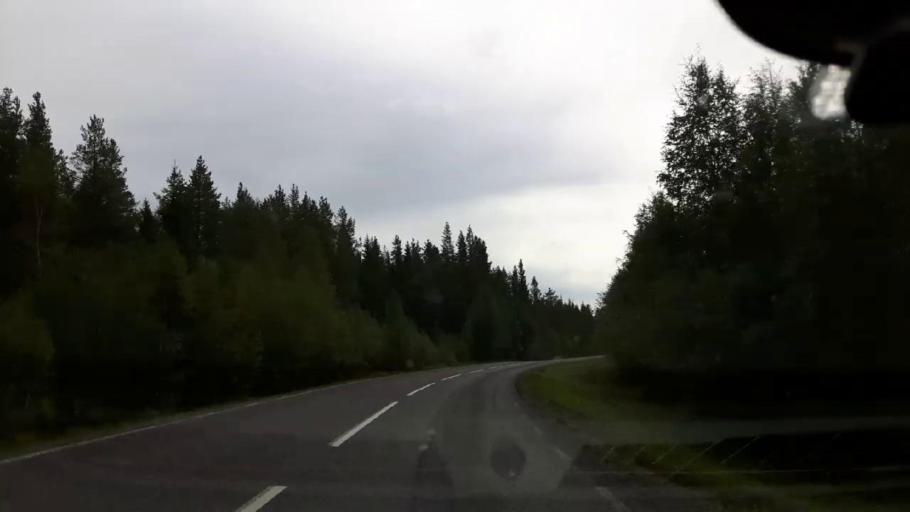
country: SE
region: Jaemtland
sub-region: Ragunda Kommun
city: Hammarstrand
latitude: 63.0613
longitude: 15.9275
